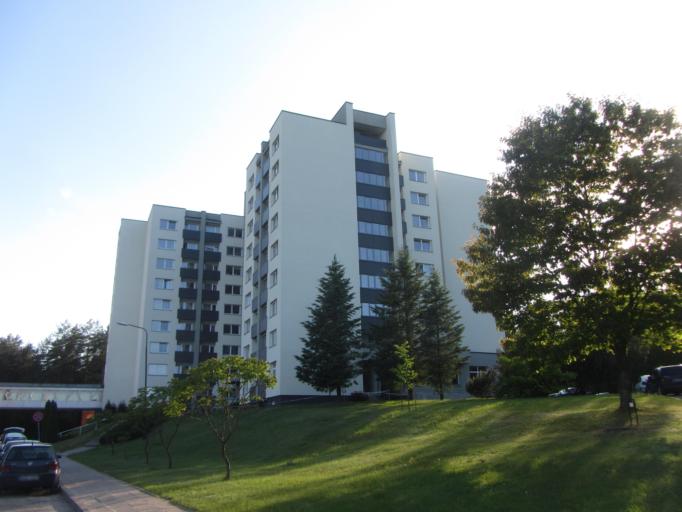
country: LT
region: Vilnius County
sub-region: Vilnius
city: Fabijoniskes
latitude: 54.7287
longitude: 25.2622
